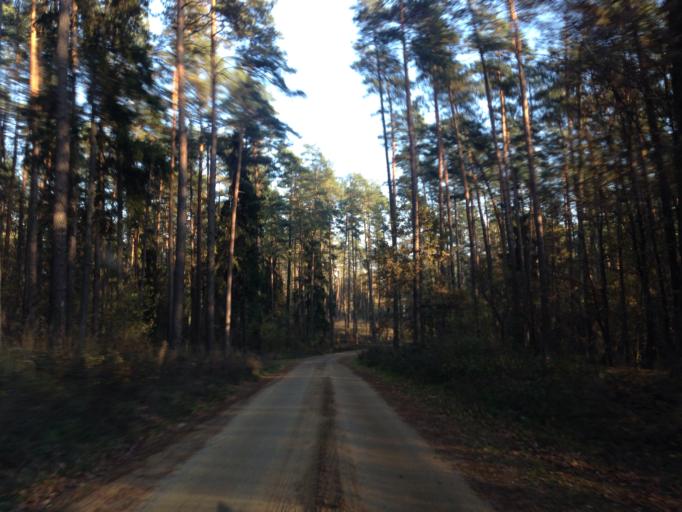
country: PL
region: Kujawsko-Pomorskie
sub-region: Powiat brodnicki
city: Gorzno
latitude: 53.1616
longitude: 19.6816
